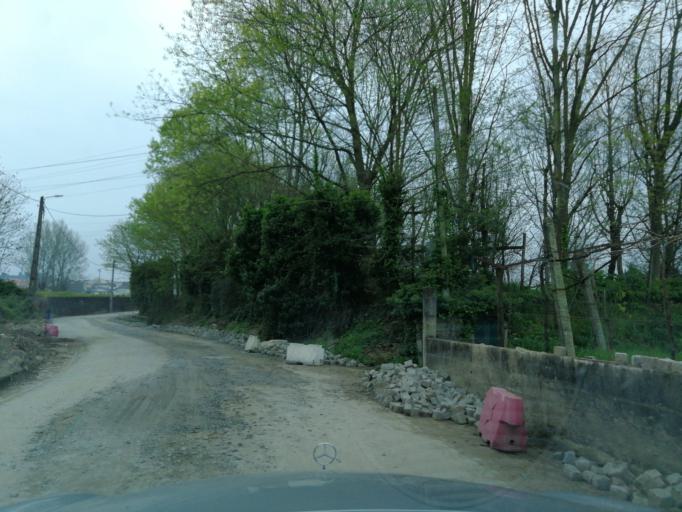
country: PT
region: Braga
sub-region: Braga
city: Braga
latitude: 41.5737
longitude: -8.4372
